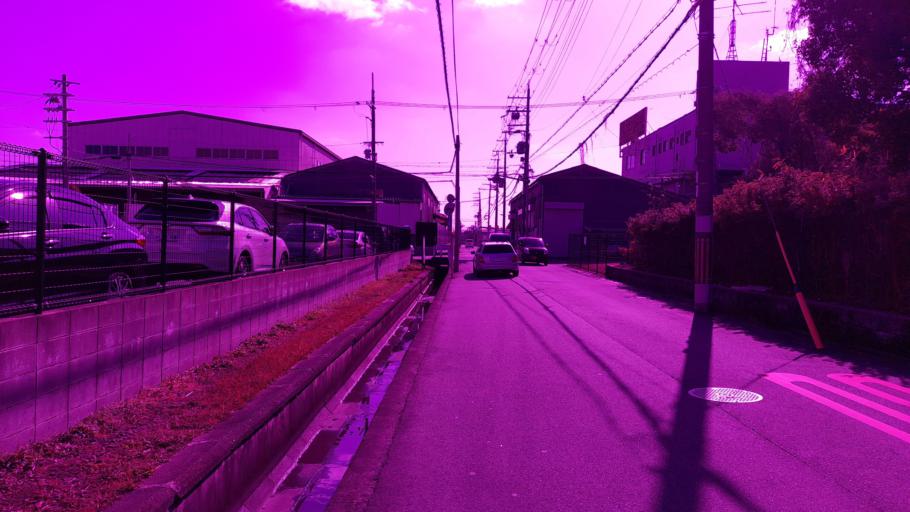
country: JP
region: Osaka
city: Toyonaka
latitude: 34.7737
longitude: 135.4554
